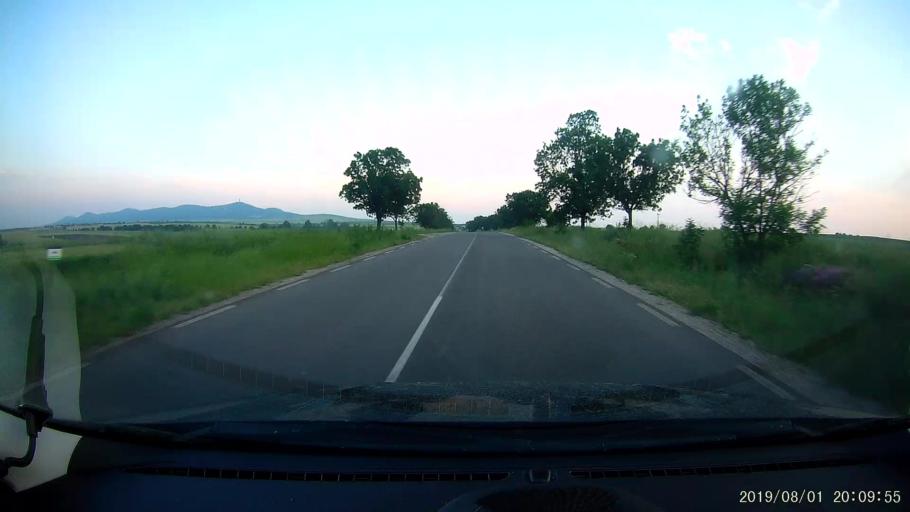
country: BG
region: Yambol
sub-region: Obshtina Yambol
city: Yambol
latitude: 42.4903
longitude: 26.5951
